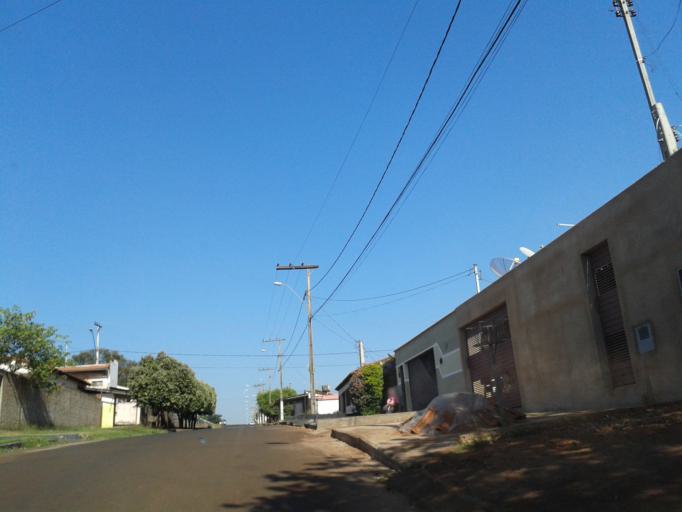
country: BR
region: Minas Gerais
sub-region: Ituiutaba
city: Ituiutaba
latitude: -18.9684
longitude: -49.4812
